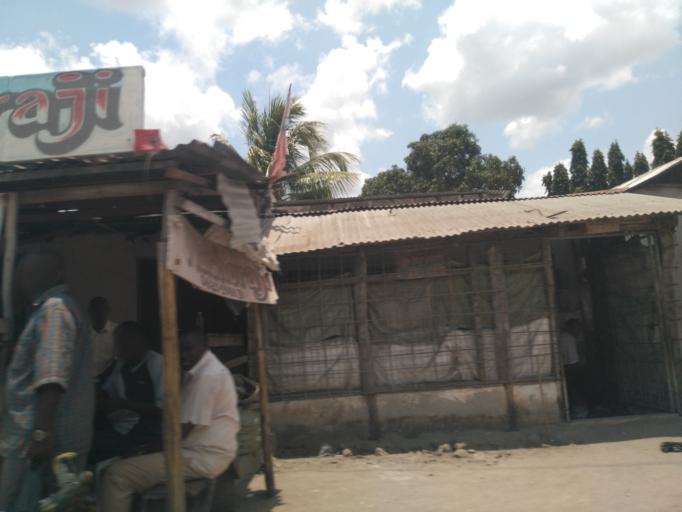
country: TZ
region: Dar es Salaam
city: Dar es Salaam
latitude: -6.8376
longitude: 39.3202
